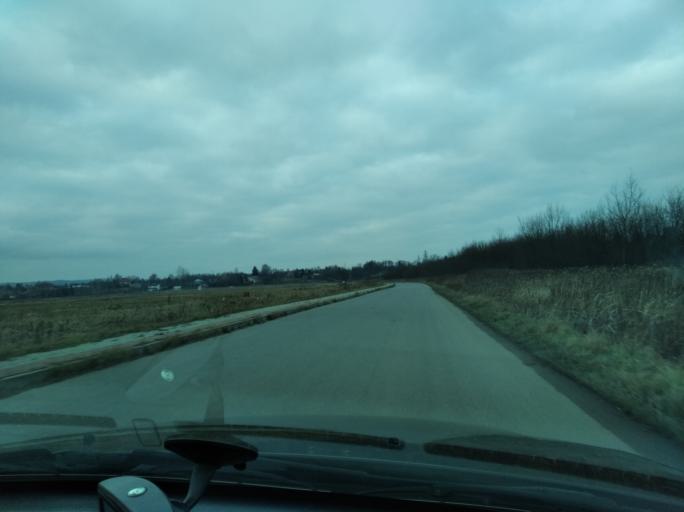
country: PL
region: Subcarpathian Voivodeship
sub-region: Powiat rzeszowski
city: Boguchwala
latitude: 49.9731
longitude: 21.9346
